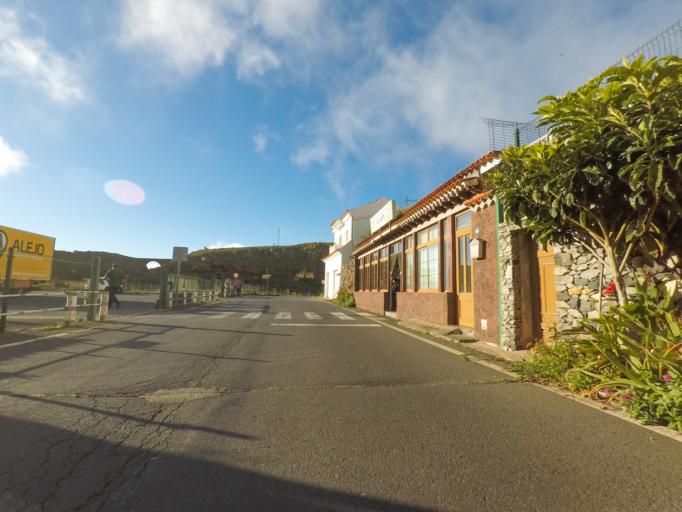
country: ES
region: Canary Islands
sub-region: Provincia de Santa Cruz de Tenerife
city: Vallehermosa
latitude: 28.1313
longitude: -17.3207
